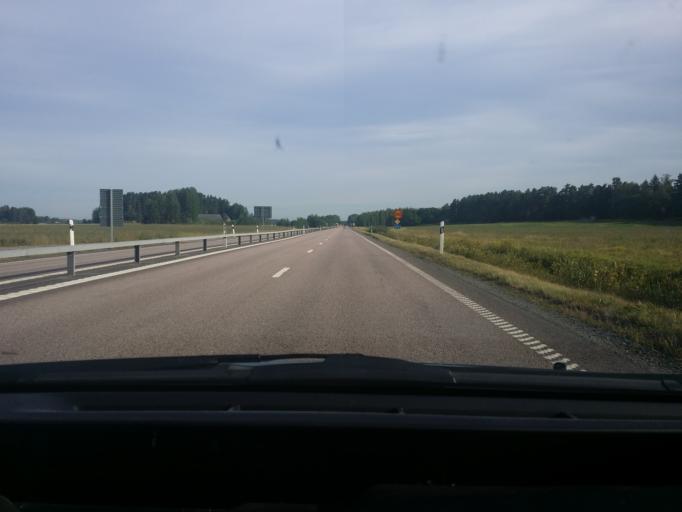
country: SE
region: Vaestmanland
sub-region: Vasteras
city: Hokasen
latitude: 59.6812
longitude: 16.5809
